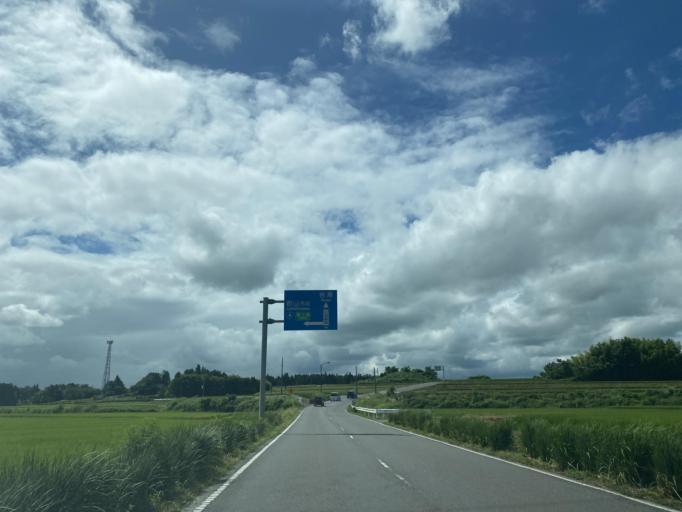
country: JP
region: Fukushima
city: Koriyama
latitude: 37.3696
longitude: 140.2940
